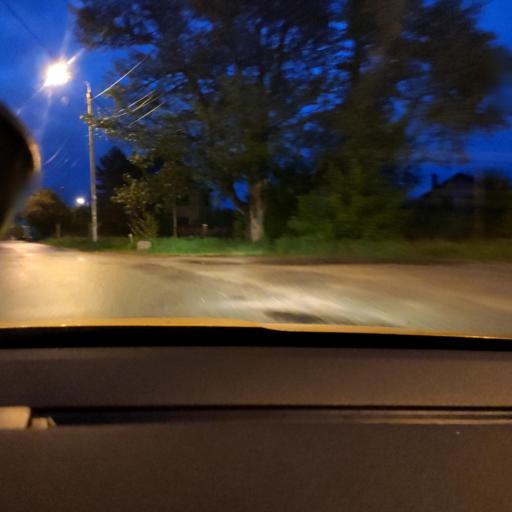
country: RU
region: Moskovskaya
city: Dmitrov
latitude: 56.3469
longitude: 37.5398
